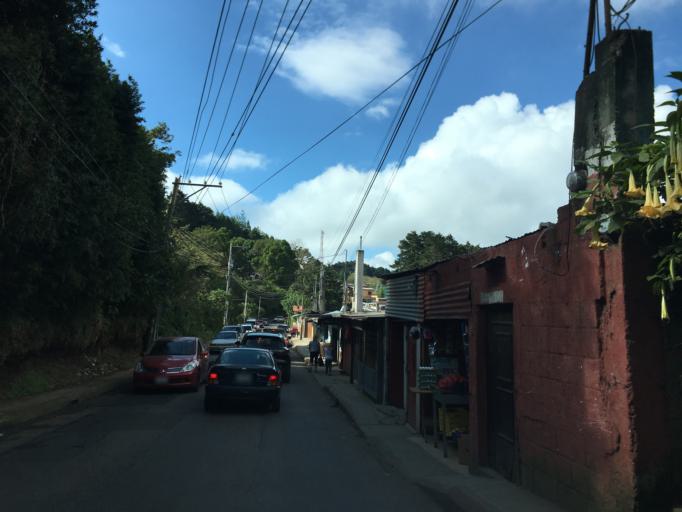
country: GT
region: Guatemala
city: San Jose Pinula
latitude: 14.5635
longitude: -90.4367
